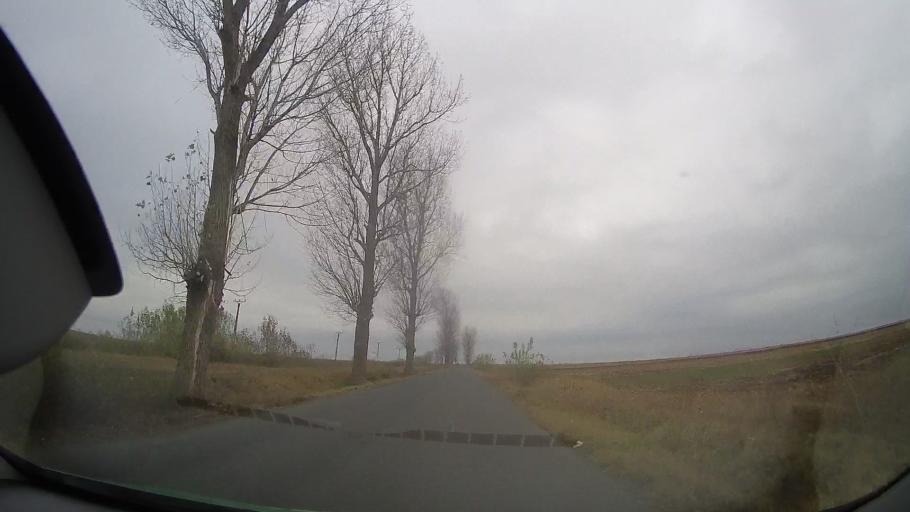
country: RO
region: Braila
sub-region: Comuna Rosiori
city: Rosiori
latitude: 44.8181
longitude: 27.3606
